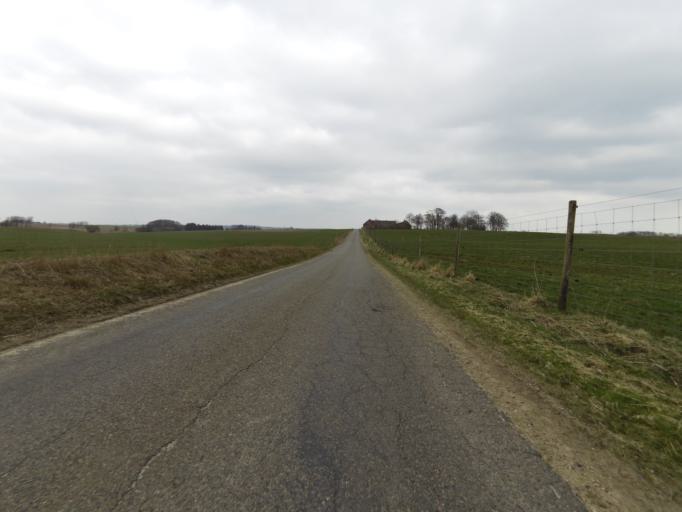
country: DK
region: Central Jutland
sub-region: Holstebro Kommune
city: Vinderup
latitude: 56.4257
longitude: 8.7161
